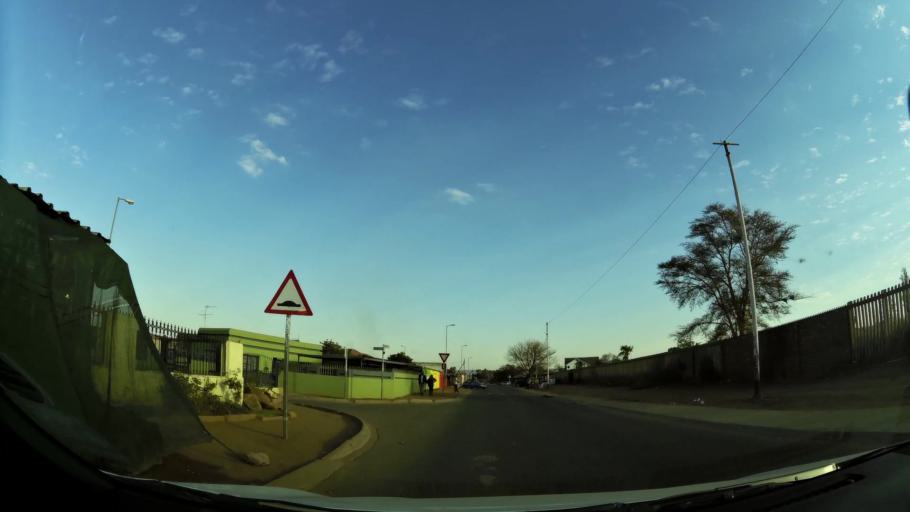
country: ZA
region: Gauteng
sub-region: City of Tshwane Metropolitan Municipality
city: Cullinan
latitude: -25.7112
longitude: 28.3650
